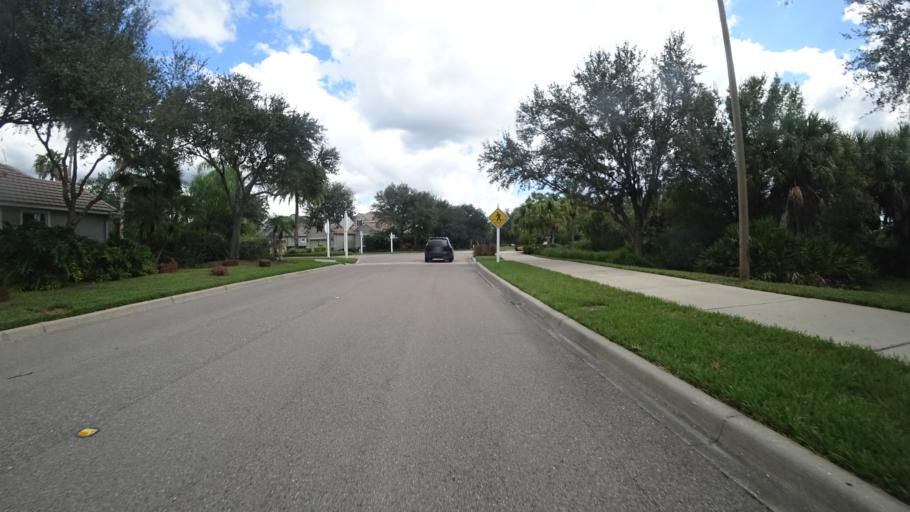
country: US
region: Florida
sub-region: Sarasota County
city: The Meadows
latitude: 27.4066
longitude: -82.4259
